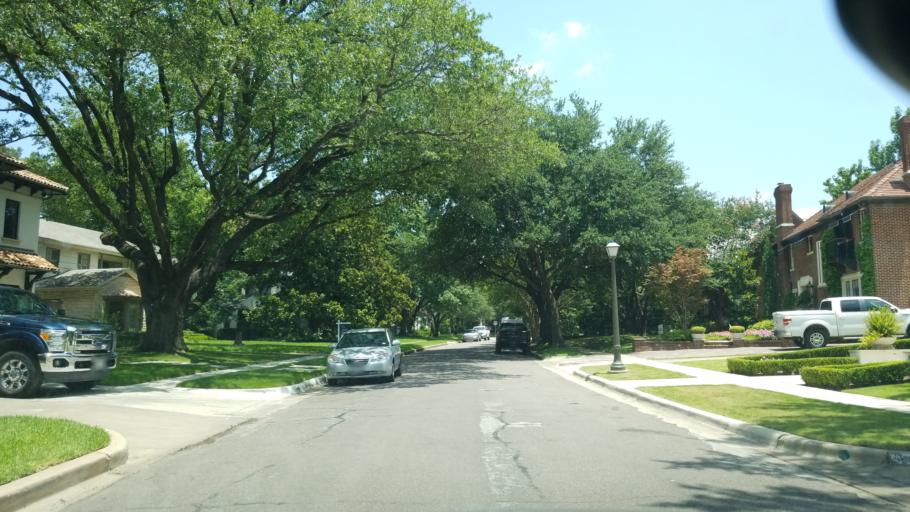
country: US
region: Texas
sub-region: Dallas County
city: Highland Park
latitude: 32.8289
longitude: -96.8109
